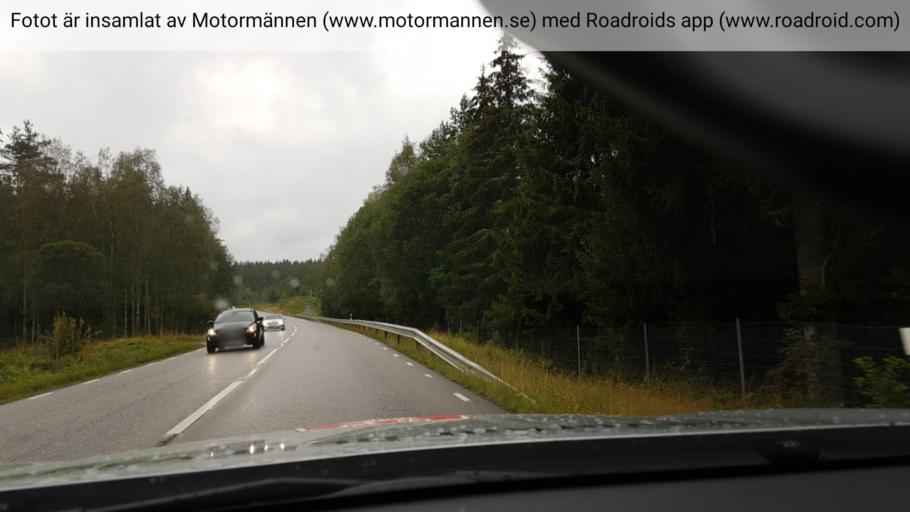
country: SE
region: Vaestra Goetaland
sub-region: Bengtsfors Kommun
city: Billingsfors
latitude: 58.9669
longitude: 12.2341
